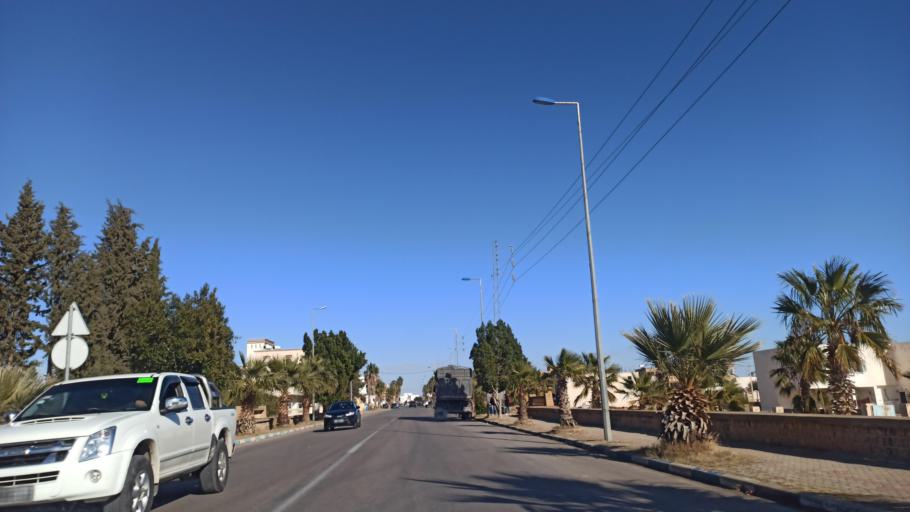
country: TN
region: Sidi Bu Zayd
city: Jilma
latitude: 35.2670
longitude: 9.4146
